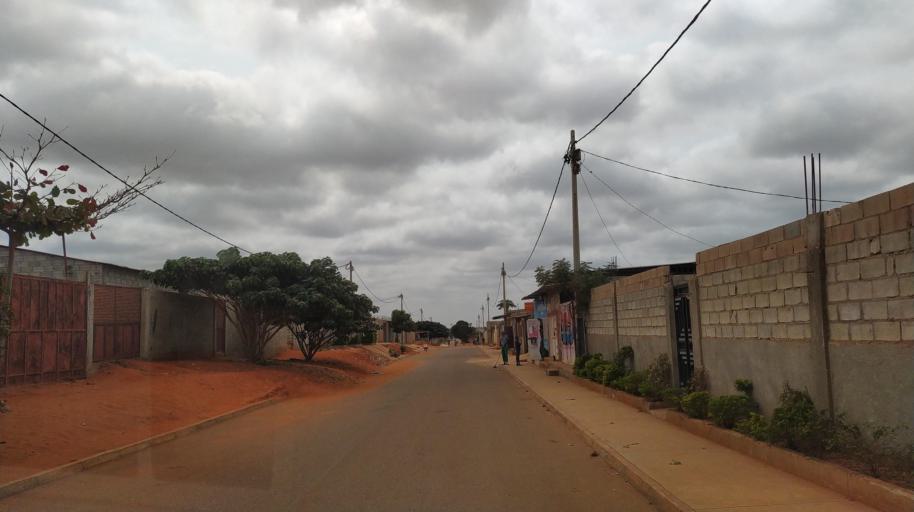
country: AO
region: Luanda
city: Luanda
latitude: -9.0712
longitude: 13.4262
